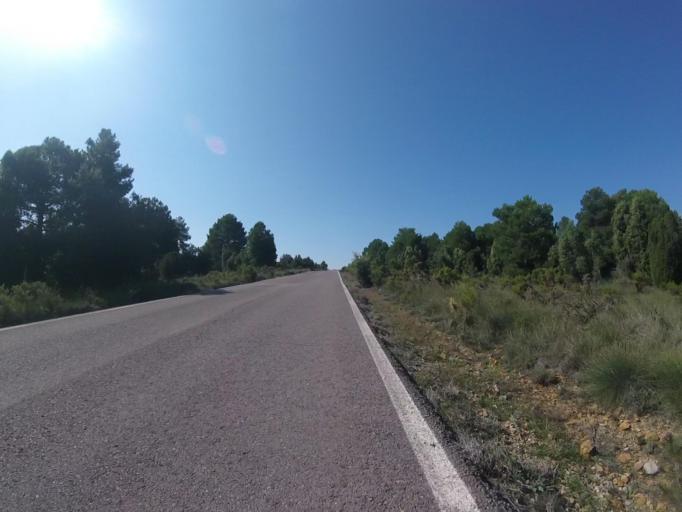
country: ES
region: Valencia
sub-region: Provincia de Castello
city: Benafigos
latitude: 40.2825
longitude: -0.2388
